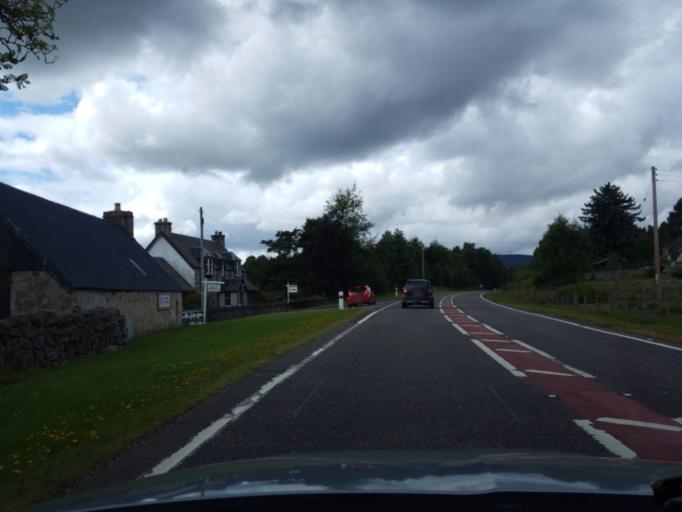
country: GB
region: Scotland
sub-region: Highland
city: Aviemore
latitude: 57.2609
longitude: -3.7425
